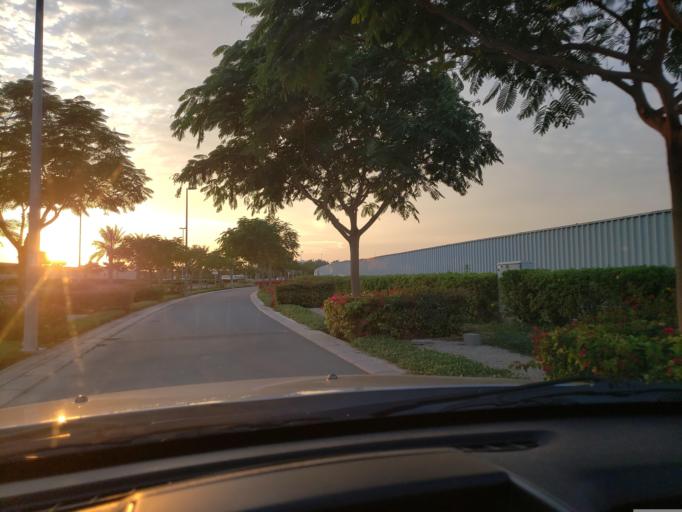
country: AE
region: Dubai
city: Dubai
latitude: 25.0141
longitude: 55.2653
